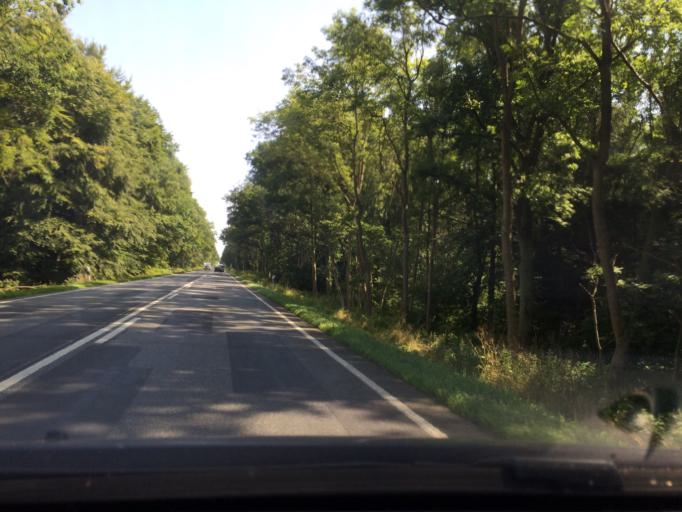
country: DE
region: Mecklenburg-Vorpommern
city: Sehlen
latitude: 54.3805
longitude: 13.3480
